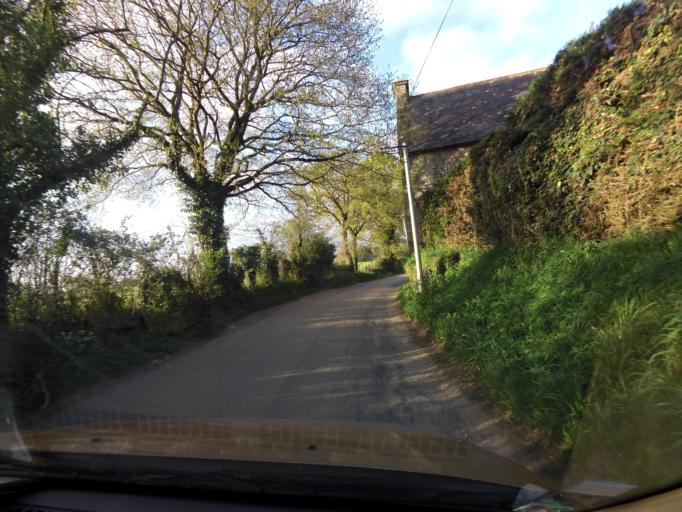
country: FR
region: Brittany
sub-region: Departement du Morbihan
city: Arradon
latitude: 47.6383
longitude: -2.8106
